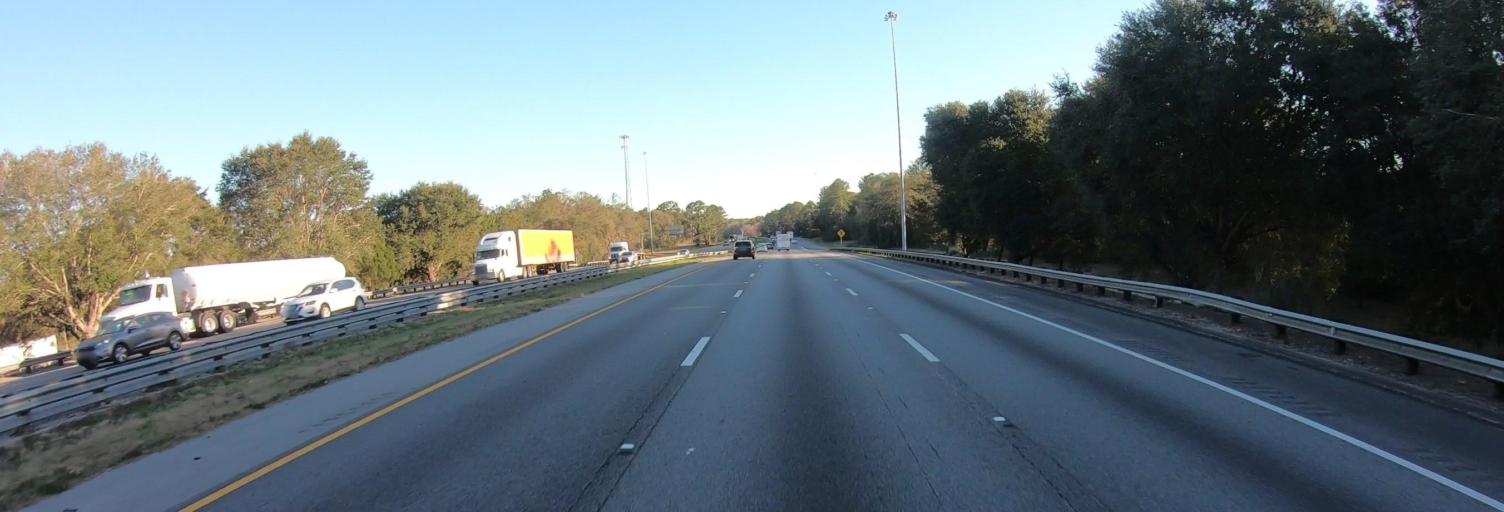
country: US
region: Florida
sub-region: Alachua County
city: Gainesville
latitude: 29.4965
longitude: -82.2950
